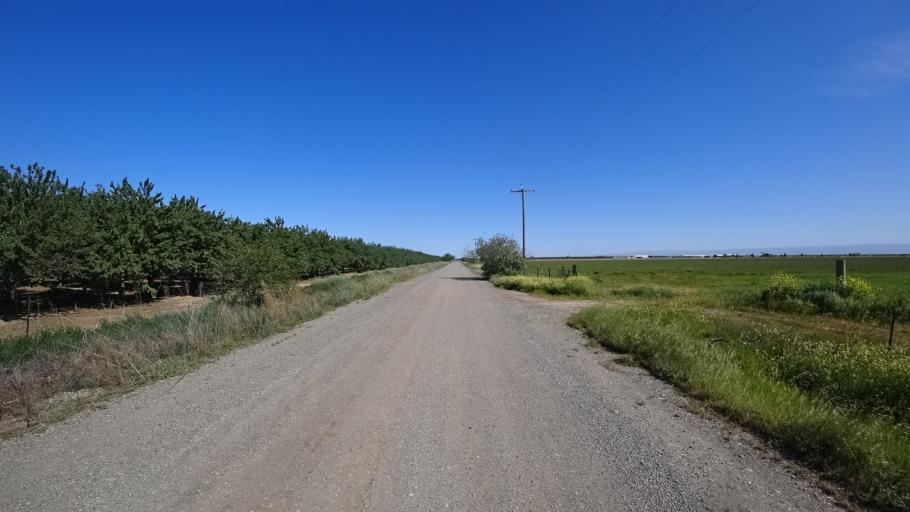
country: US
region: California
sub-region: Glenn County
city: Orland
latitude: 39.6485
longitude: -122.1597
